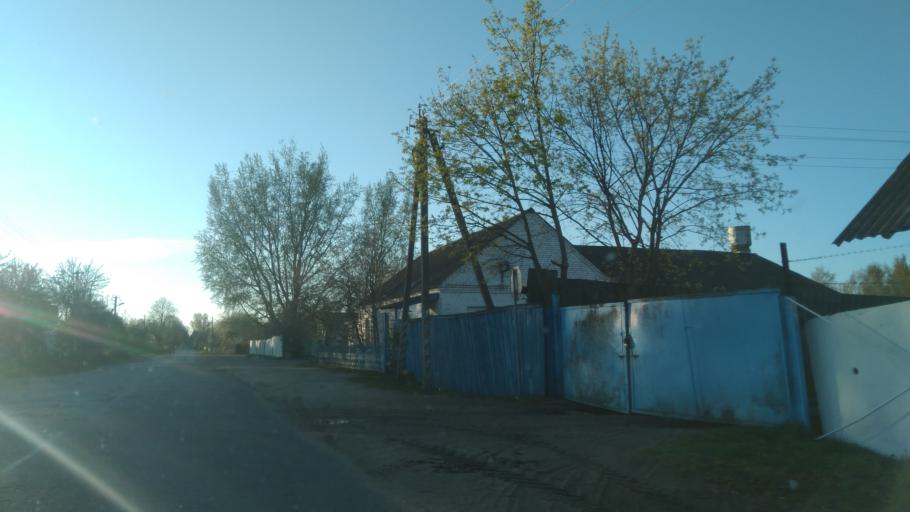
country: BY
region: Minsk
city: Haradzyeya
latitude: 53.3612
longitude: 26.5339
